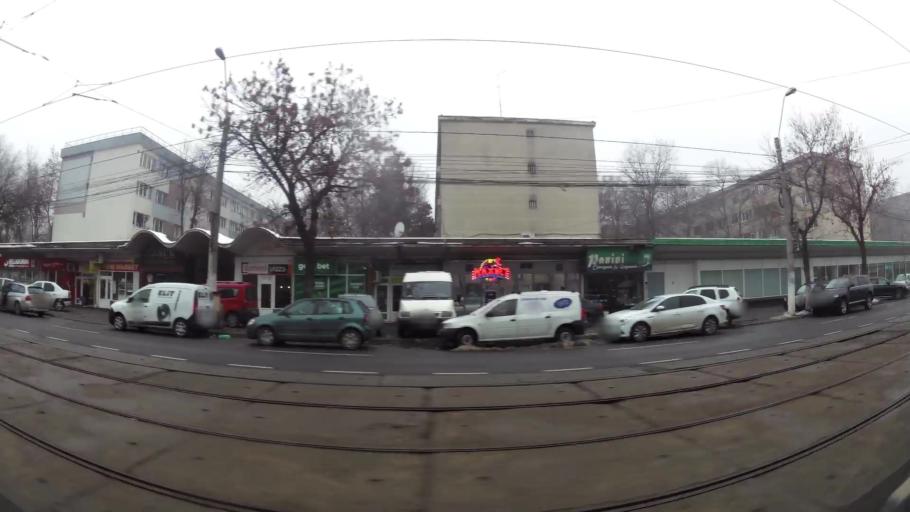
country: RO
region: Ilfov
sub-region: Comuna Chiajna
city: Rosu
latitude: 44.4629
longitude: 26.0429
